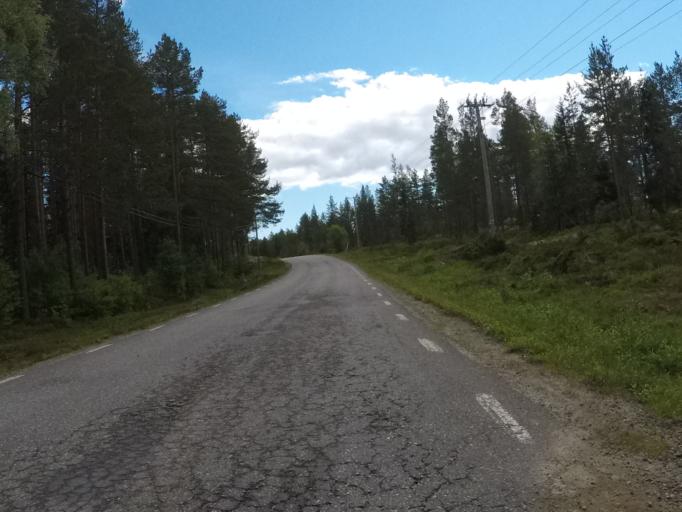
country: SE
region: Vaesterbotten
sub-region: Robertsfors Kommun
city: Robertsfors
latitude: 63.9929
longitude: 20.8196
